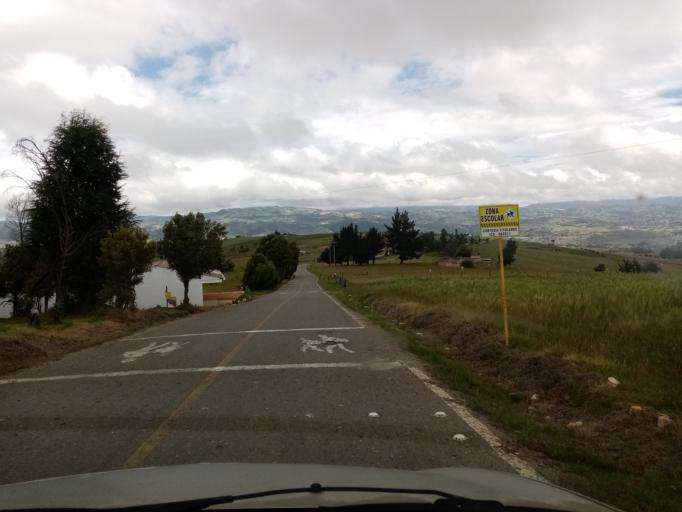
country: CO
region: Boyaca
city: Siachoque
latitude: 5.5649
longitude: -73.2898
